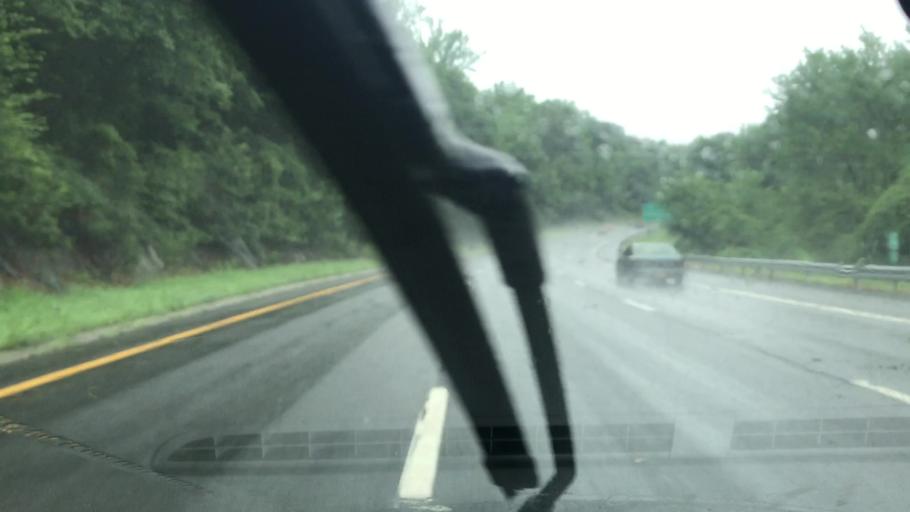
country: US
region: New York
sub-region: Westchester County
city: Yorktown Heights
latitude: 41.2326
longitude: -73.8112
